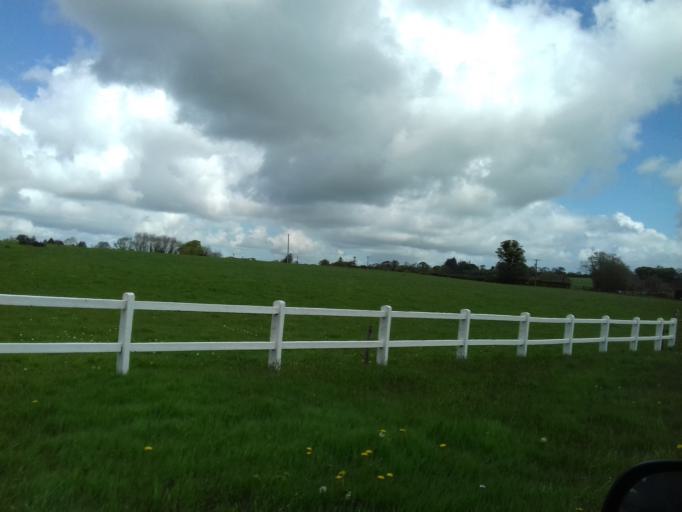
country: IE
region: Leinster
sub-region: Loch Garman
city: Castlebridge
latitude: 52.3828
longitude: -6.5018
